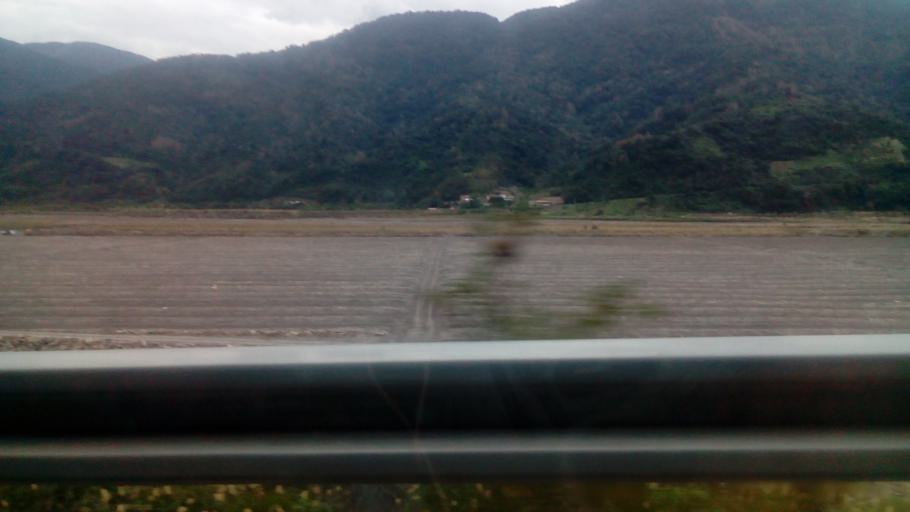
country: TW
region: Taiwan
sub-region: Yilan
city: Yilan
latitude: 24.5962
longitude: 121.5115
